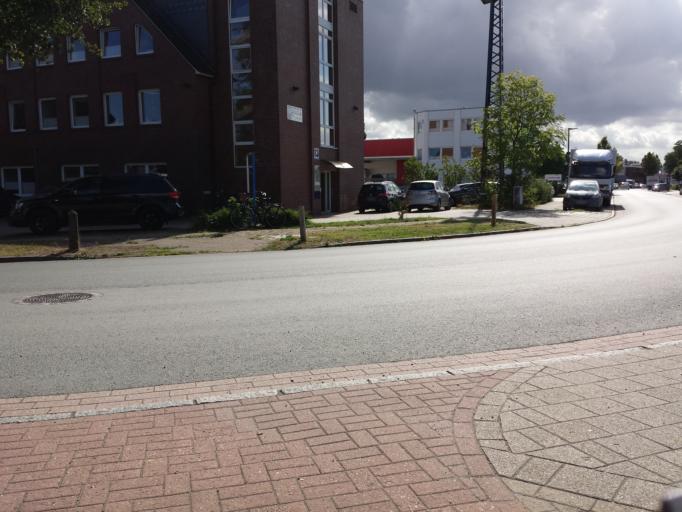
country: DE
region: Bremen
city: Bremen
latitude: 53.0493
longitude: 8.8434
